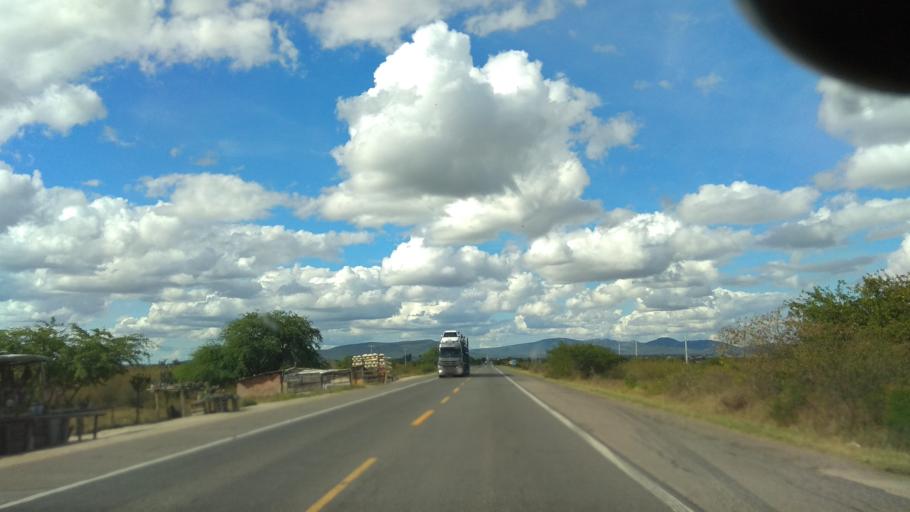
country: BR
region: Bahia
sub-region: Castro Alves
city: Castro Alves
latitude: -12.7035
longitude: -39.7189
